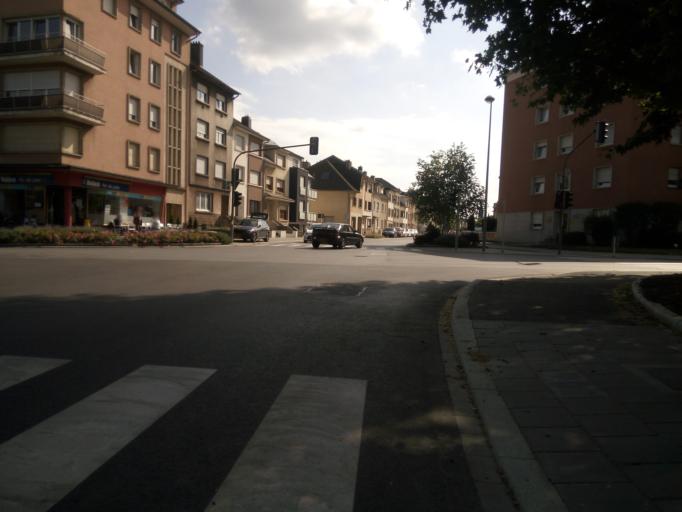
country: LU
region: Luxembourg
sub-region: Canton d'Esch-sur-Alzette
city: Esch-sur-Alzette
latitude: 49.5048
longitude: 5.9848
